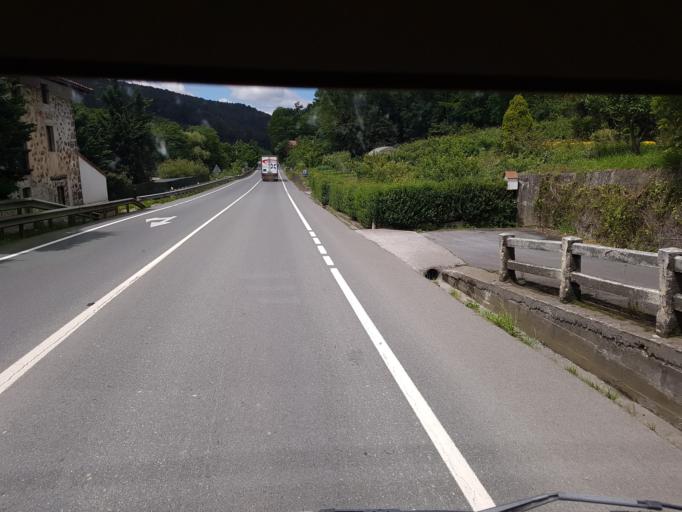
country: ES
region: Basque Country
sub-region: Bizkaia
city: Galdakao
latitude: 43.2306
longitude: -2.7825
